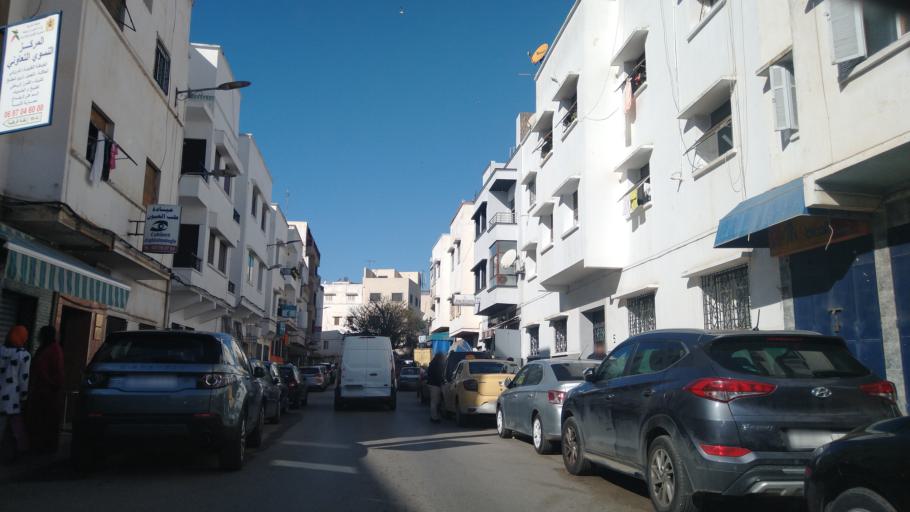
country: MA
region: Rabat-Sale-Zemmour-Zaer
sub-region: Rabat
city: Rabat
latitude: 34.0345
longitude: -6.8196
